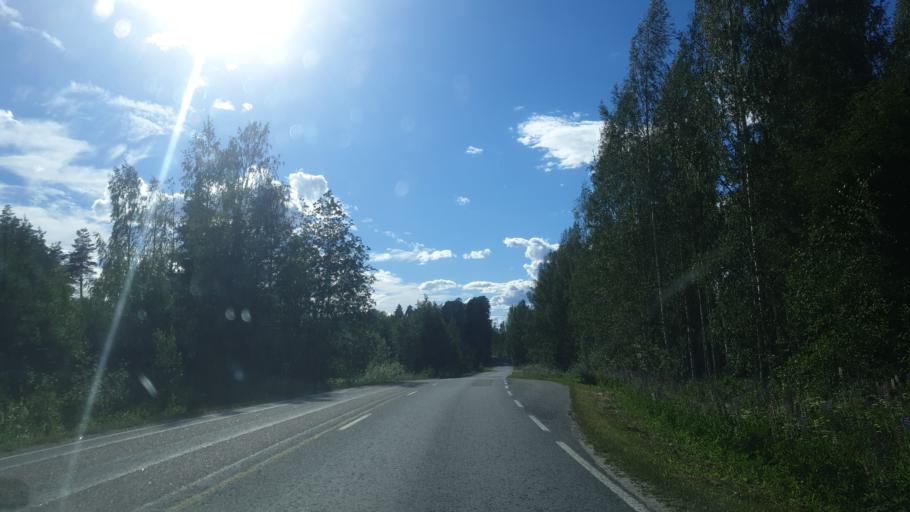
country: FI
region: Southern Savonia
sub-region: Mikkeli
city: Pertunmaa
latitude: 61.5233
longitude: 26.5480
